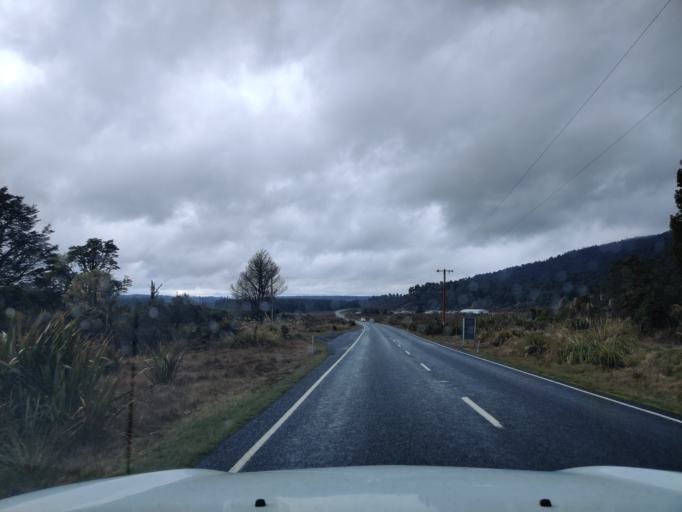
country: NZ
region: Manawatu-Wanganui
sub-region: Ruapehu District
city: Waiouru
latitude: -39.2339
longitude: 175.3928
